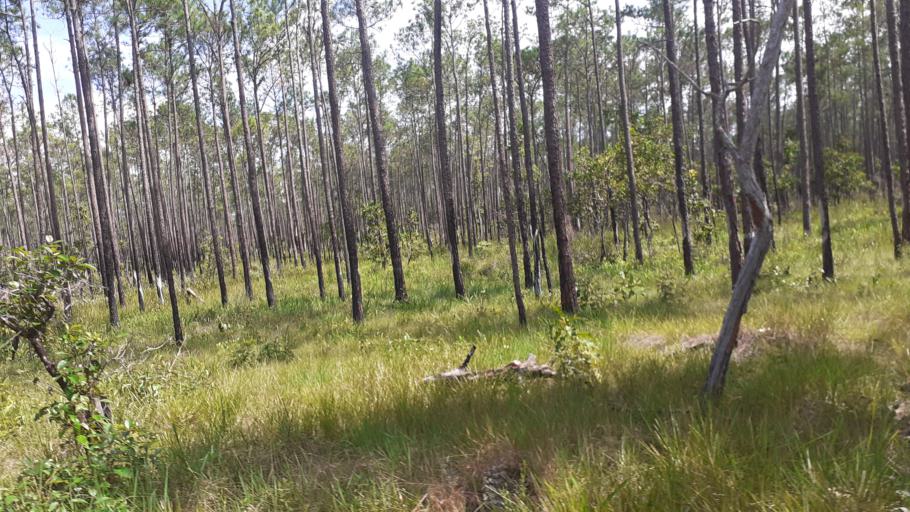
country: HN
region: Gracias a Dios
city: Auka
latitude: 14.7454
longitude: -83.7539
